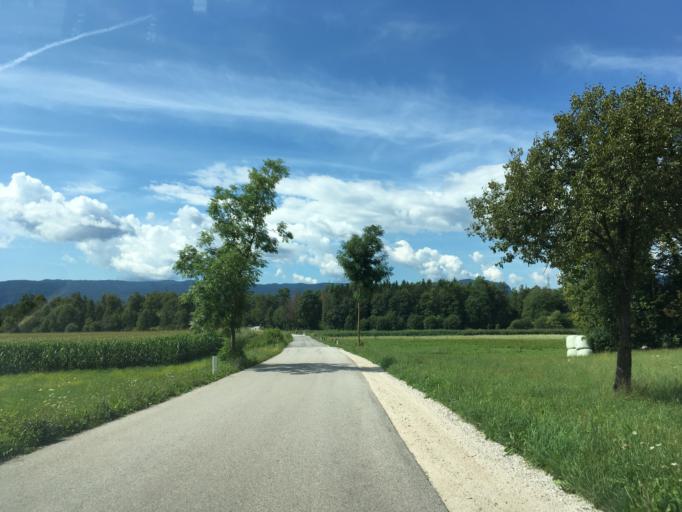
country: SI
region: Radovljica
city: Lesce
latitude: 46.3800
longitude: 14.1730
